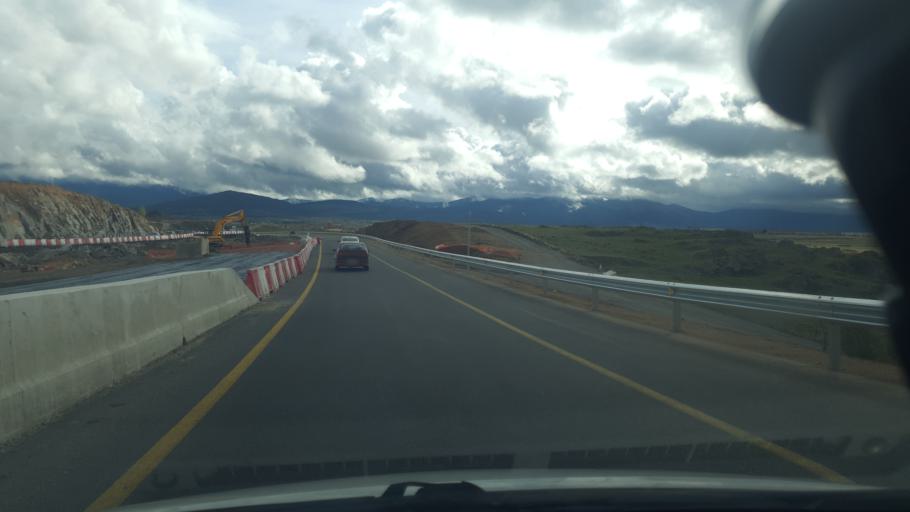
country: ES
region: Castille and Leon
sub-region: Provincia de Segovia
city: San Cristobal de Segovia
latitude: 40.9511
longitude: -4.0907
